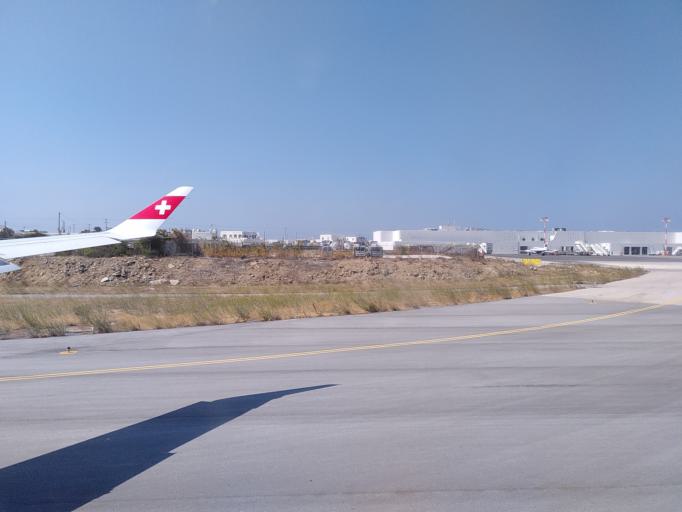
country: GR
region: South Aegean
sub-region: Nomos Kykladon
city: Mykonos
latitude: 37.4338
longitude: 25.3489
